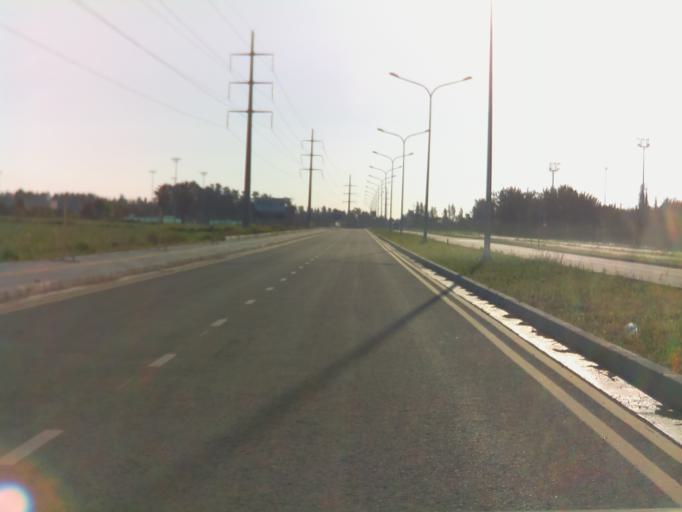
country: CY
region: Pafos
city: Paphos
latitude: 34.7462
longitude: 32.4393
